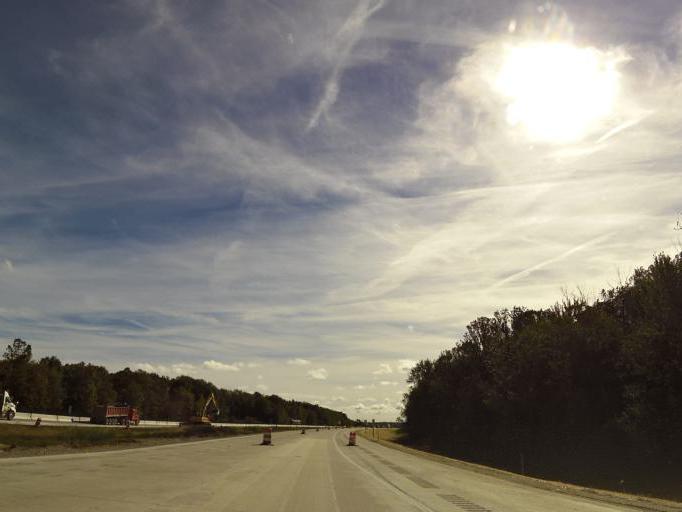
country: US
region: Michigan
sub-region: Macomb County
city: Memphis
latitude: 42.9792
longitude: -82.7547
